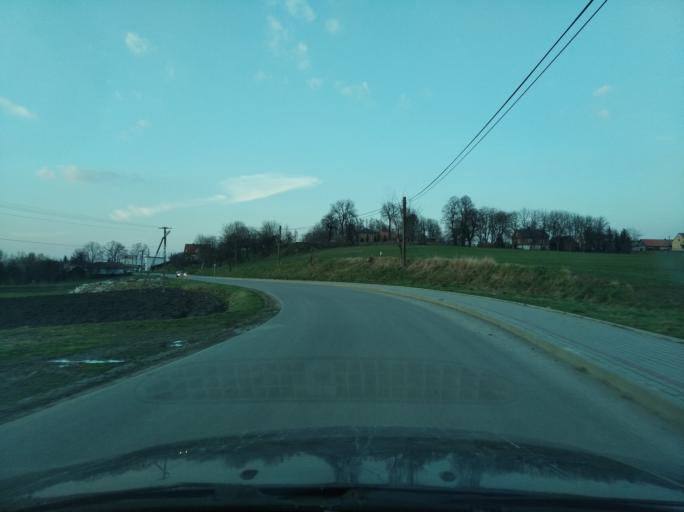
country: PL
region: Subcarpathian Voivodeship
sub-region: Powiat przeworski
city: Zurawiczki
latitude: 50.0160
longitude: 22.5015
